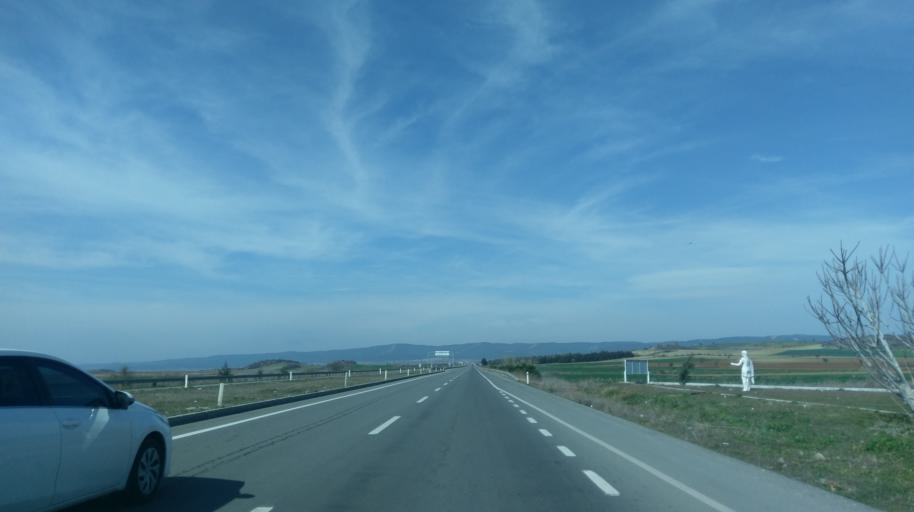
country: TR
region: Canakkale
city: Evrese
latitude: 40.6401
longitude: 26.8579
